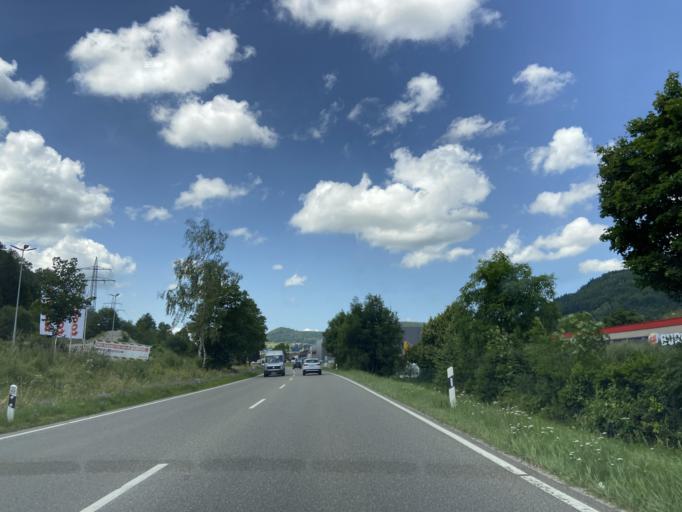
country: DE
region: Baden-Wuerttemberg
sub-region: Tuebingen Region
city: Albstadt
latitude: 48.2034
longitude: 9.0441
